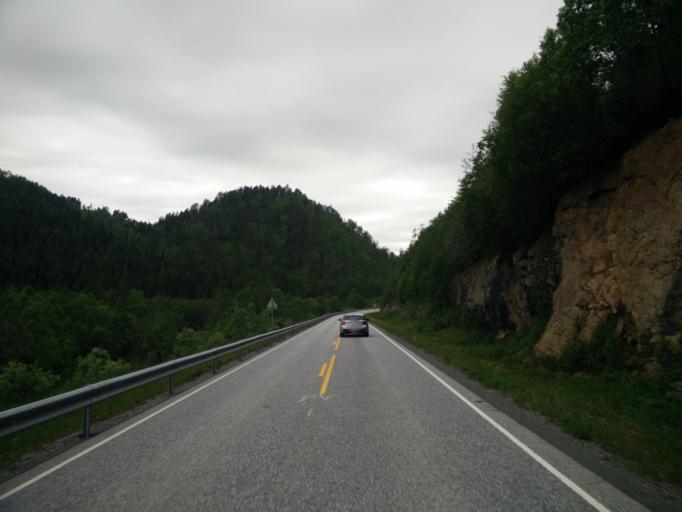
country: NO
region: Sor-Trondelag
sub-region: Hemne
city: Kyrksaeterora
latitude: 63.2106
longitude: 9.1517
